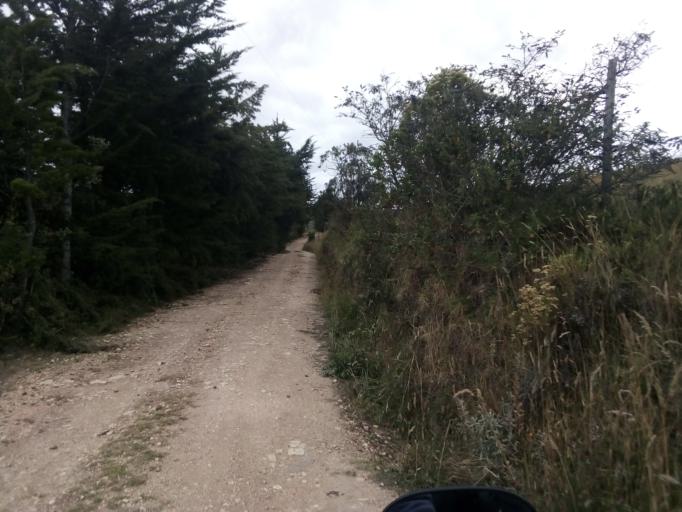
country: CO
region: Boyaca
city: Toca
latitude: 5.5899
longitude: -73.1301
